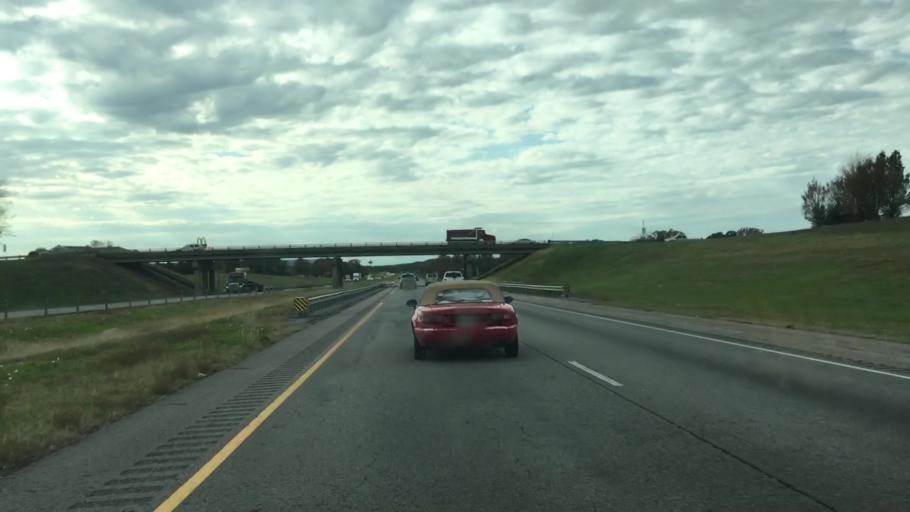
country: US
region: Arkansas
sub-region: Conway County
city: Morrilton
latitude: 35.1743
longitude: -92.7164
